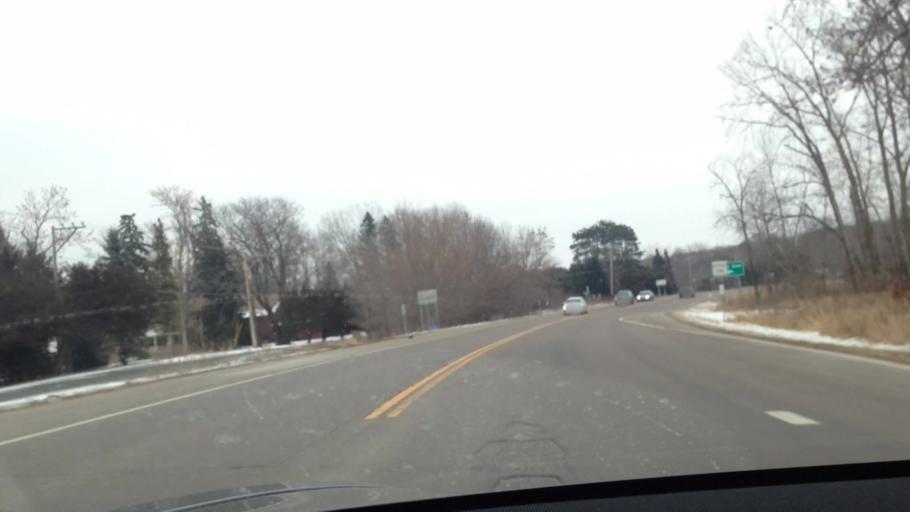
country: US
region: Minnesota
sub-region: Washington County
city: Forest Lake
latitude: 45.2630
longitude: -92.9457
